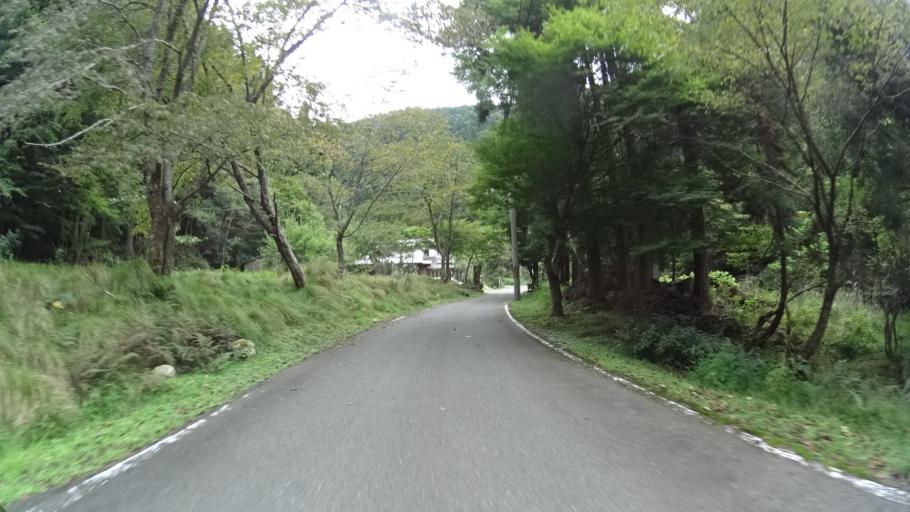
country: JP
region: Shiga Prefecture
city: Kitahama
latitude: 35.2351
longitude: 135.7856
